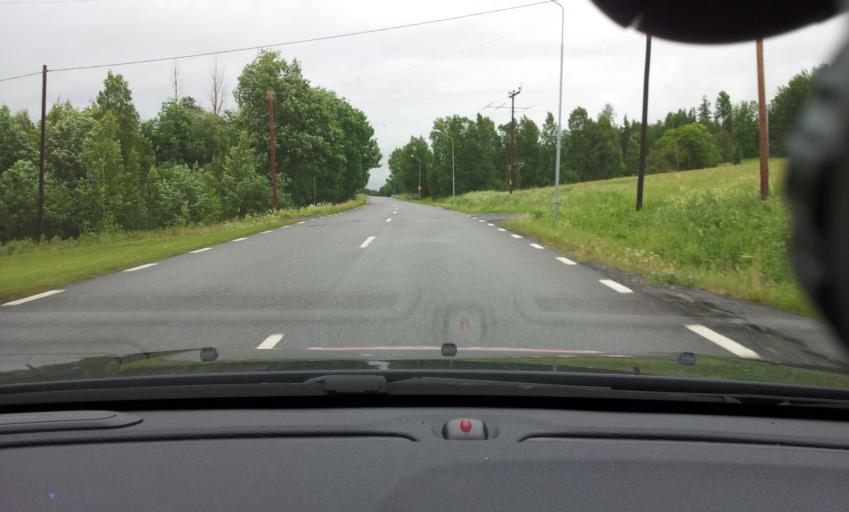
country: SE
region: Jaemtland
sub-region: Stroemsunds Kommun
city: Stroemsund
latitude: 63.5742
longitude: 15.3779
